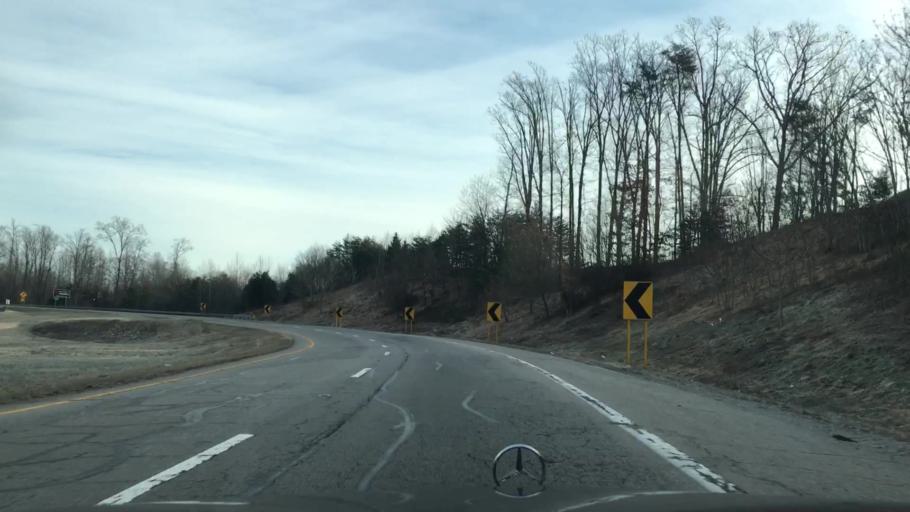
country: US
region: Virginia
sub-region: City of Danville
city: Danville
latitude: 36.5393
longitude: -79.4647
